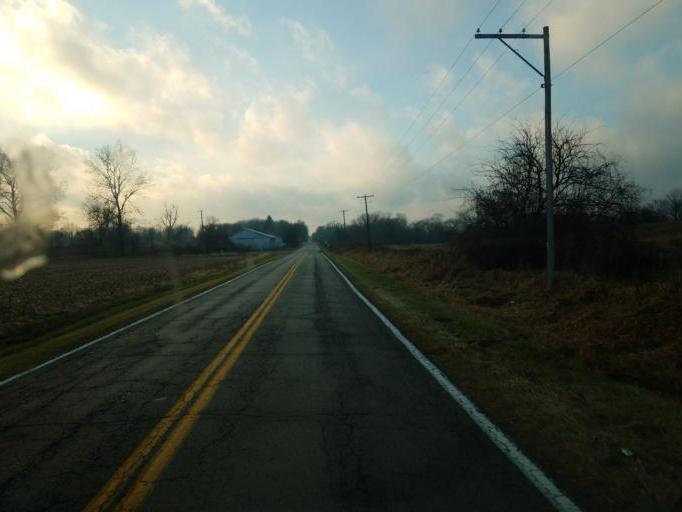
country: US
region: Ohio
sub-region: Knox County
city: Centerburg
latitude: 40.2724
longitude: -82.6377
